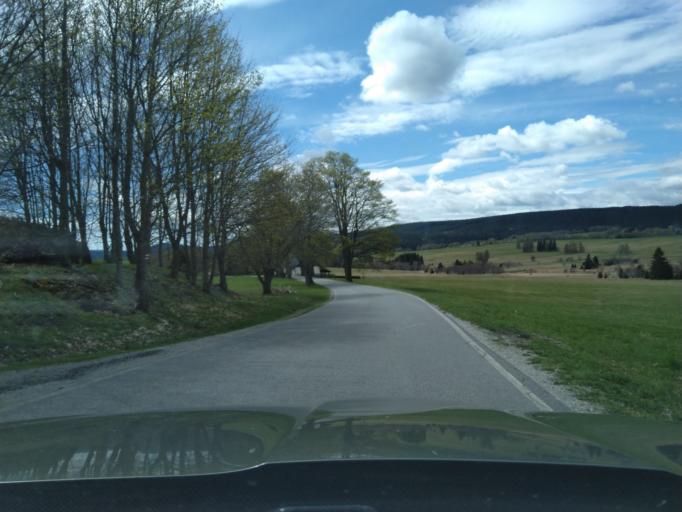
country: CZ
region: Jihocesky
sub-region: Okres Prachatice
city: Borova Lada
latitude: 49.0403
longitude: 13.6689
